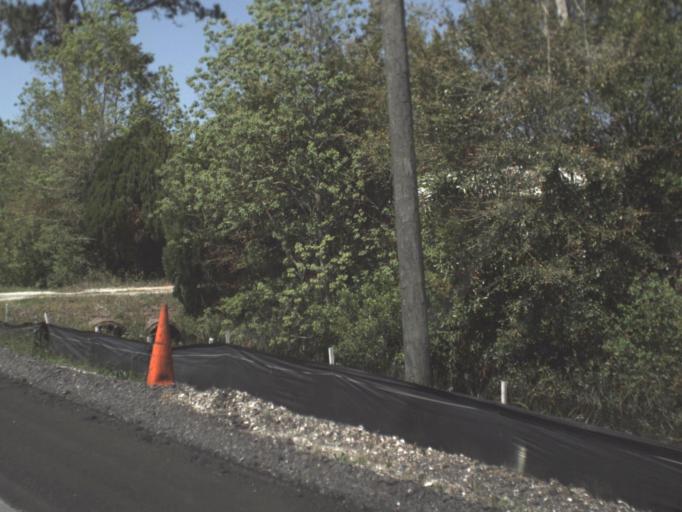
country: US
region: Florida
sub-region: Escambia County
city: Myrtle Grove
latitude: 30.3974
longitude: -87.3169
